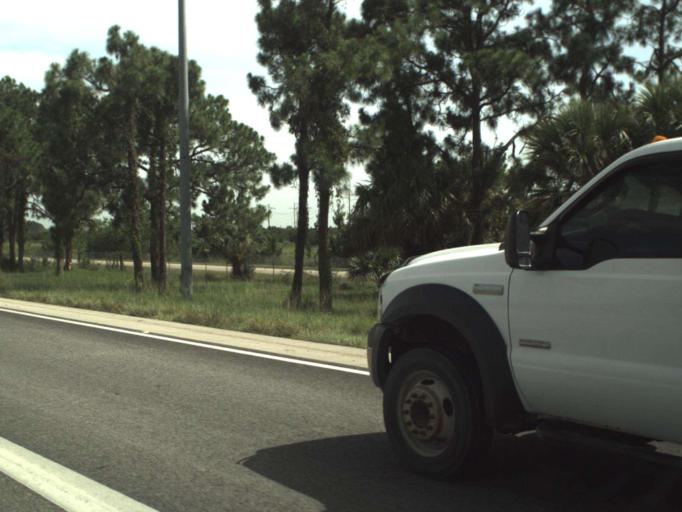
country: US
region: Florida
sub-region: Saint Lucie County
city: Lakewood Park
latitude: 27.5166
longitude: -80.4485
